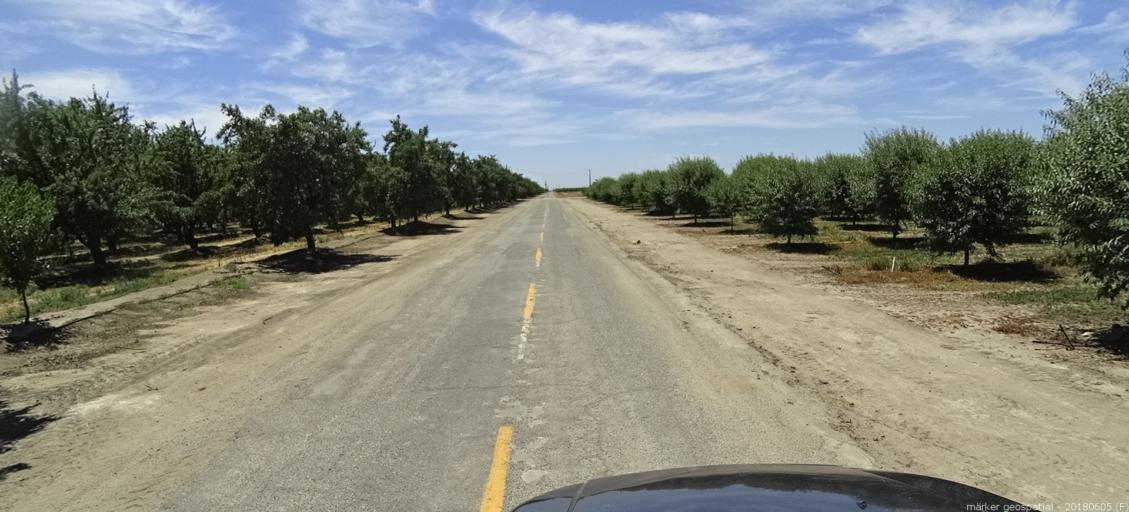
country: US
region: California
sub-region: Madera County
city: Chowchilla
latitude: 37.0907
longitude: -120.4398
